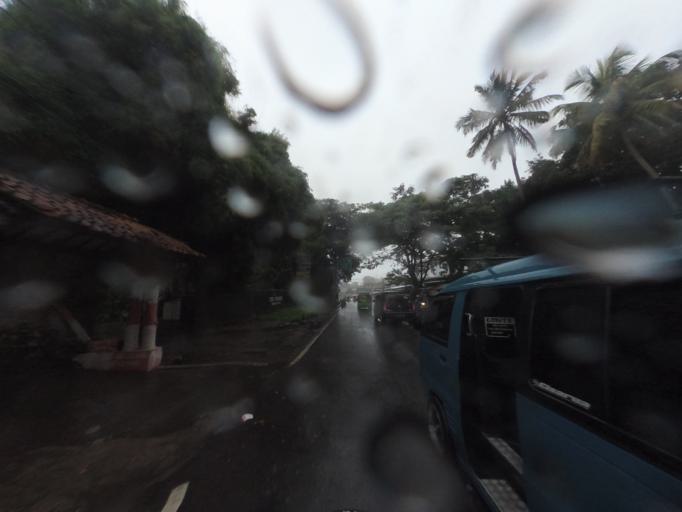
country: ID
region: West Java
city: Caringin
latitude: -6.6573
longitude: 106.8584
